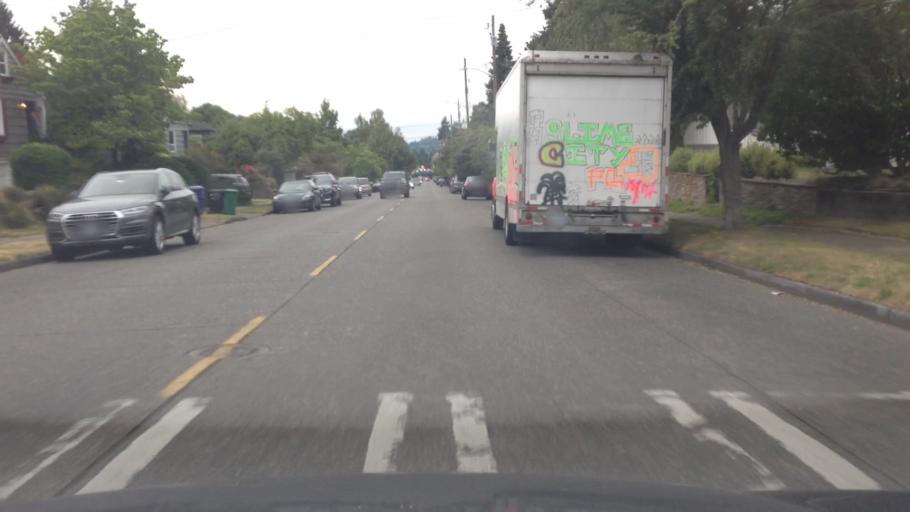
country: US
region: Washington
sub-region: King County
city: Inglewood-Finn Hill
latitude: 47.6721
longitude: -122.2849
